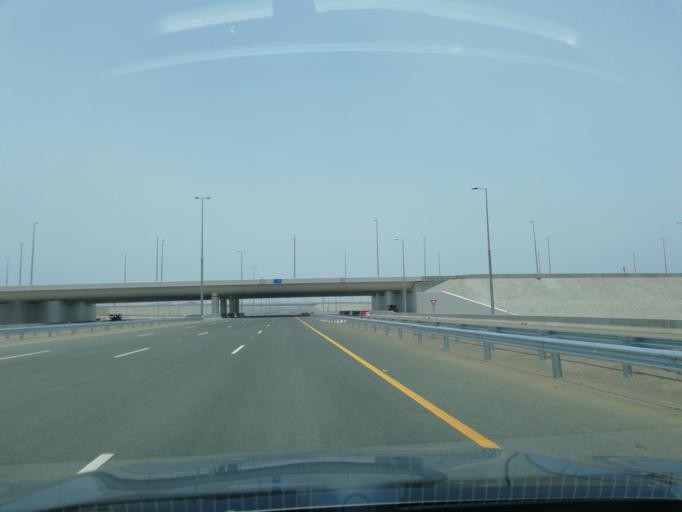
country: OM
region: Al Batinah
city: Al Liwa'
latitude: 24.4534
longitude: 56.5164
